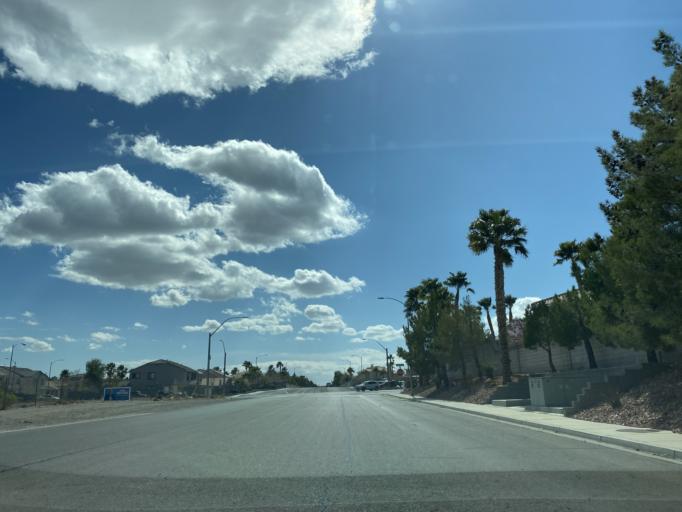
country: US
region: Nevada
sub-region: Clark County
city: Summerlin South
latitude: 36.2347
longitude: -115.2884
